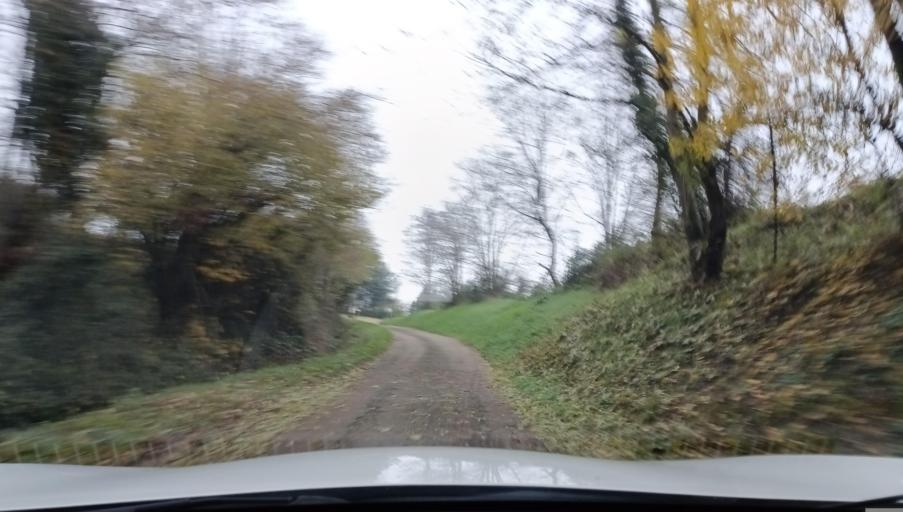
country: FR
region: Rhone-Alpes
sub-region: Departement de l'Isere
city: Chuzelles
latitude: 45.5693
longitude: 4.8707
